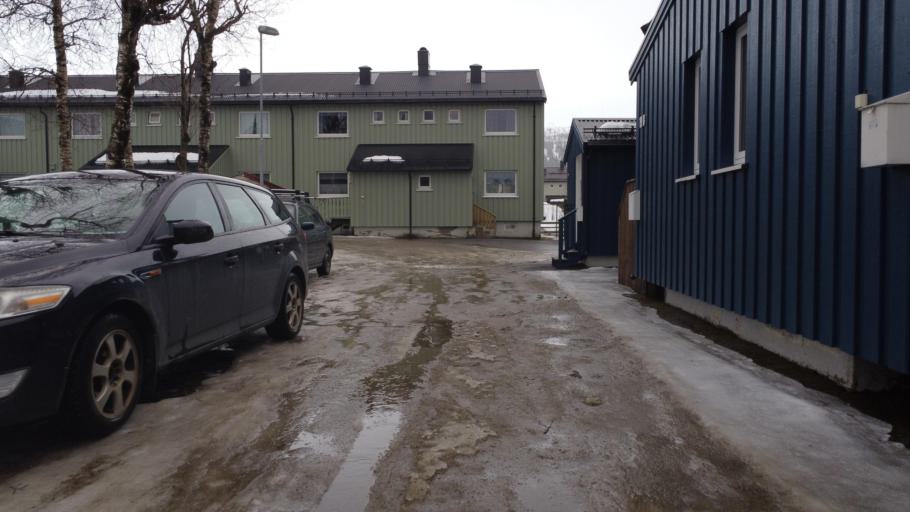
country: NO
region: Nordland
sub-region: Rana
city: Mo i Rana
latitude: 66.3171
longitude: 14.1589
